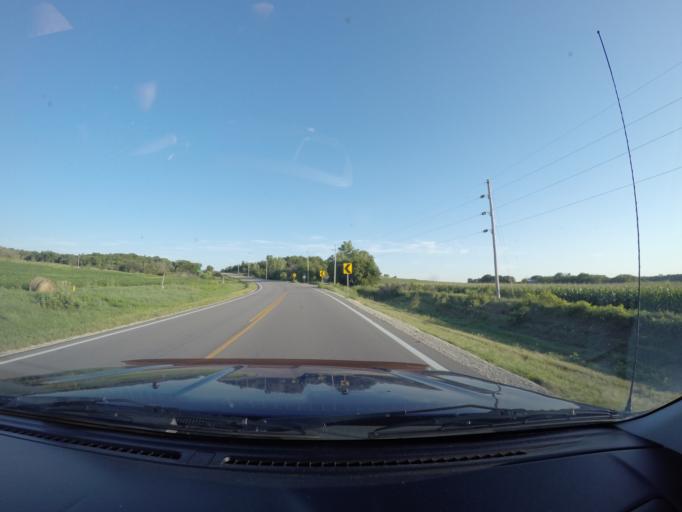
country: US
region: Kansas
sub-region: Pottawatomie County
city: Wamego
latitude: 39.1422
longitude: -96.3056
